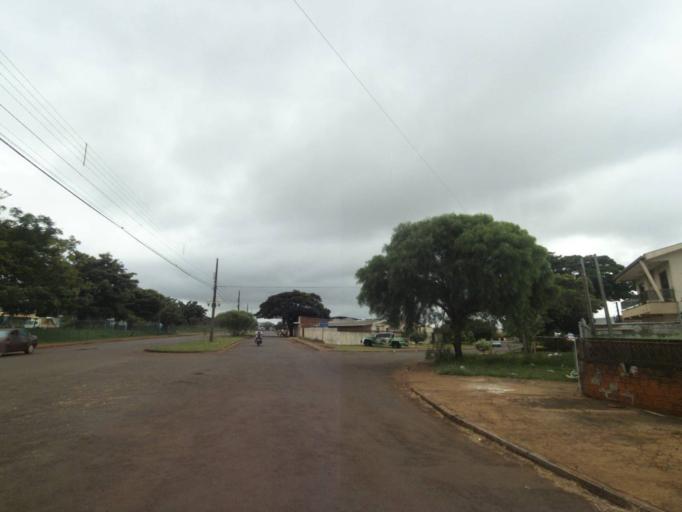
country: BR
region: Parana
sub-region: Campo Mourao
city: Campo Mourao
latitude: -24.0230
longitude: -52.3561
